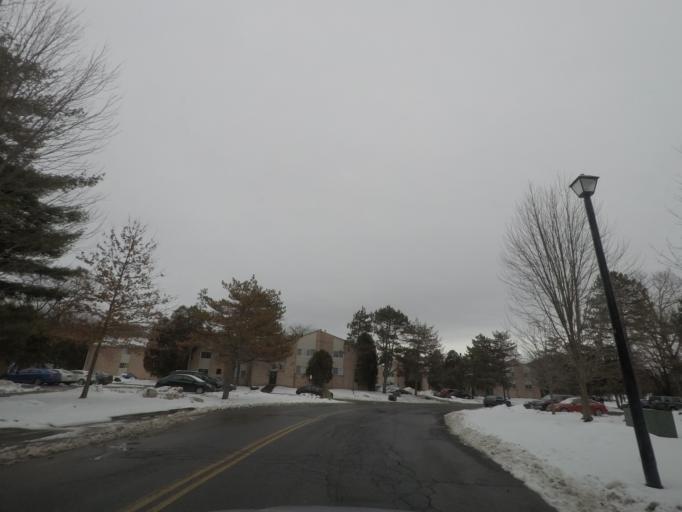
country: US
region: New York
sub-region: Albany County
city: Watervliet
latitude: 42.7345
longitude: -73.7314
